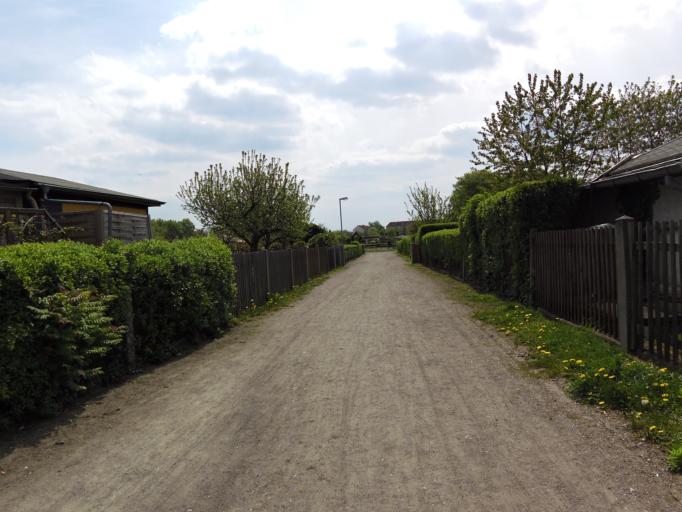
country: DE
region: Saxony
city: Leipzig
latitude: 51.3722
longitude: 12.3916
